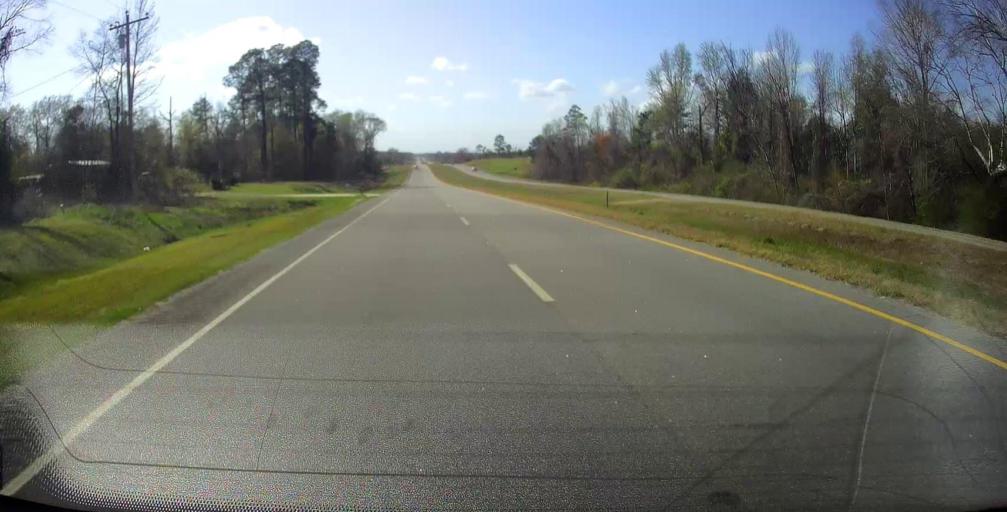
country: US
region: Georgia
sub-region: Dodge County
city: Eastman
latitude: 32.2029
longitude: -83.2849
